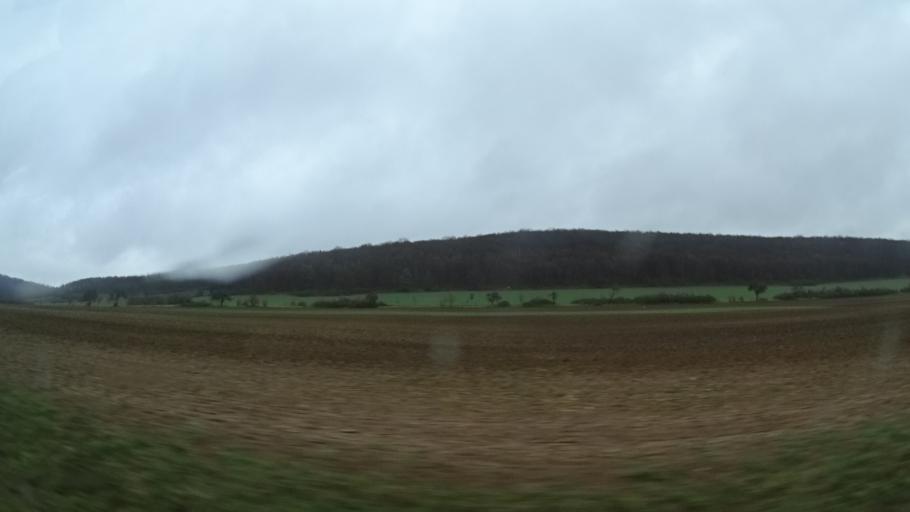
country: DE
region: Thuringia
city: Juchsen
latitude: 50.4717
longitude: 10.5241
